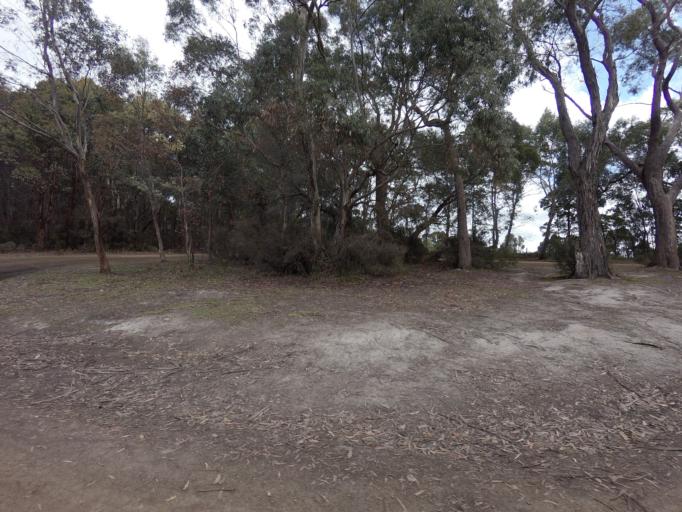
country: AU
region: Tasmania
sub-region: Huon Valley
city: Geeveston
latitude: -43.4375
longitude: 146.9890
